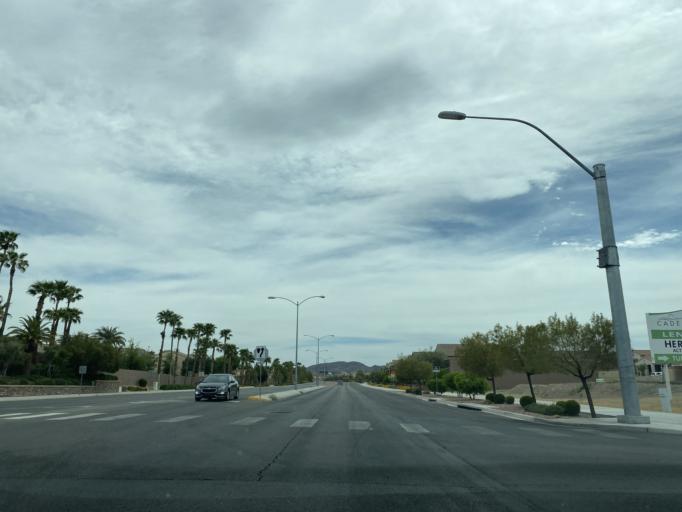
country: US
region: Nevada
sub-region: Clark County
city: Henderson
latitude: 36.0711
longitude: -114.9679
